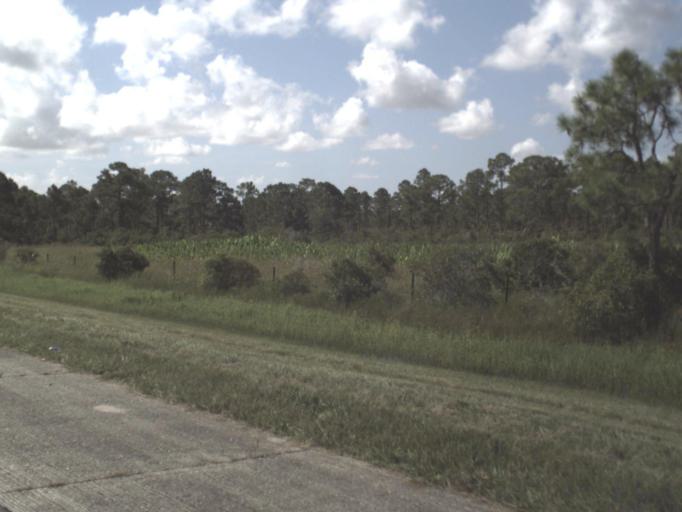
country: US
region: Florida
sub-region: Lee County
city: Burnt Store Marina
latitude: 26.8168
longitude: -81.9614
